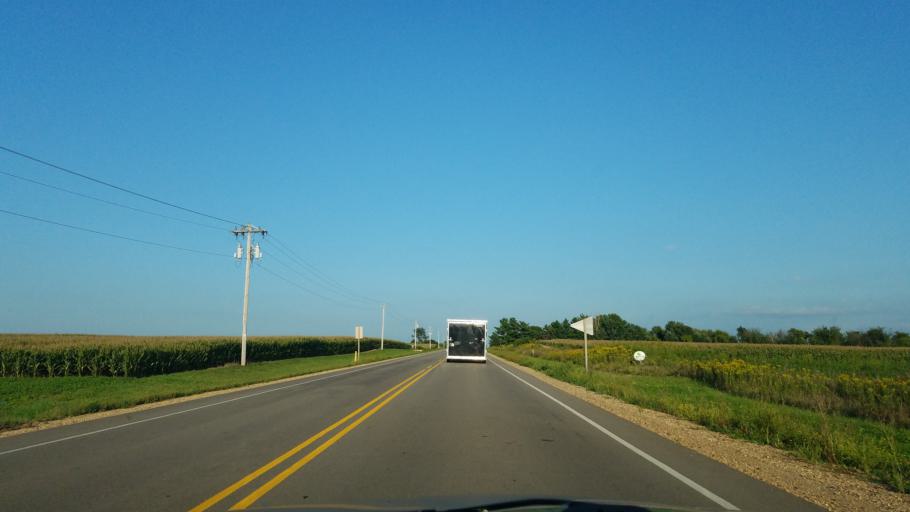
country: US
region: Wisconsin
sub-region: Saint Croix County
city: New Richmond
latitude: 45.0790
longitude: -92.5326
